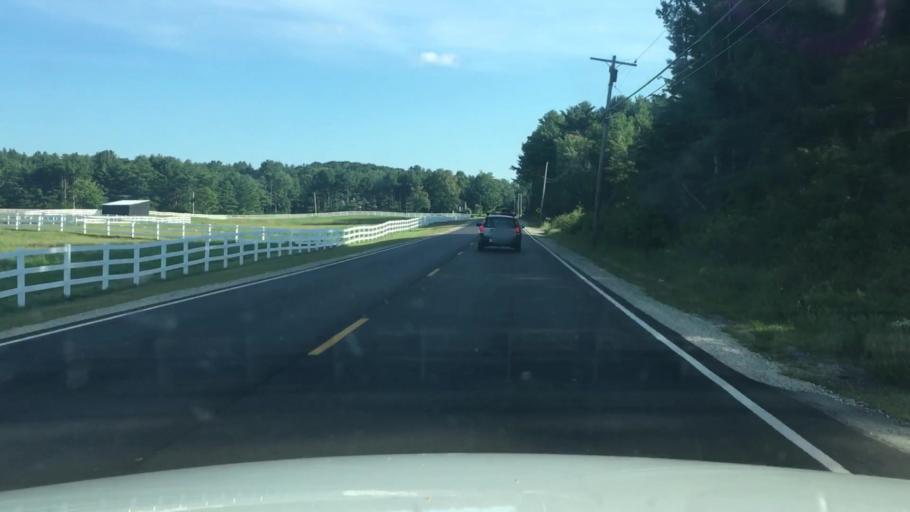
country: US
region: Maine
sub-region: Cumberland County
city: Cumberland Center
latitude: 43.7843
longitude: -70.3043
